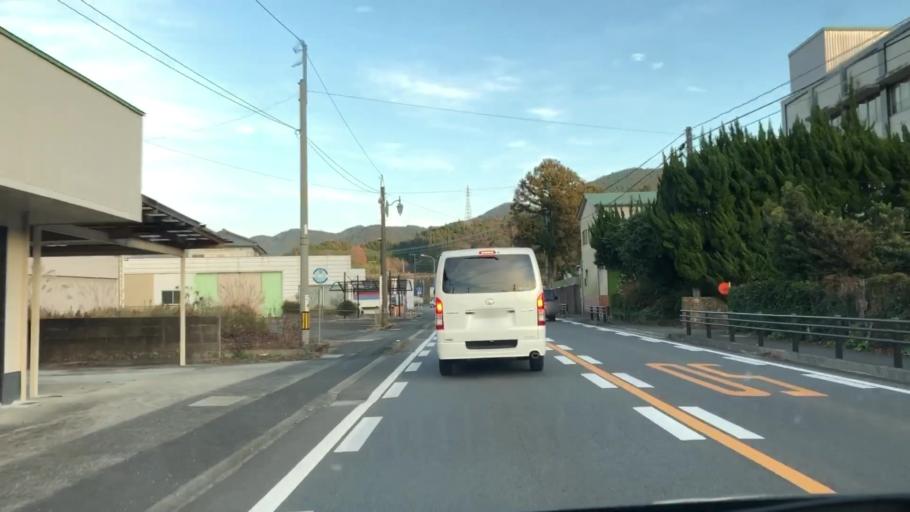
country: JP
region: Kumamoto
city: Minamata
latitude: 32.2313
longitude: 130.4588
